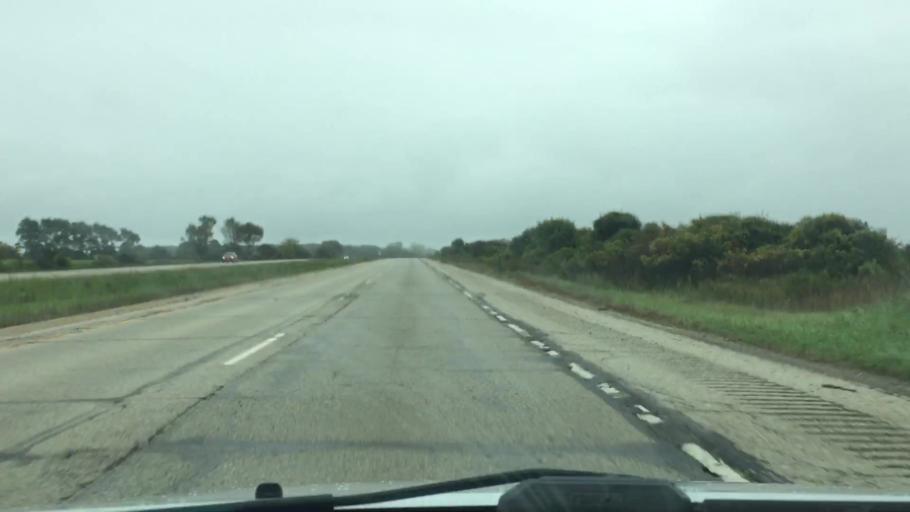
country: US
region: Wisconsin
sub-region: Walworth County
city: Como
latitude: 42.6384
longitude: -88.4865
